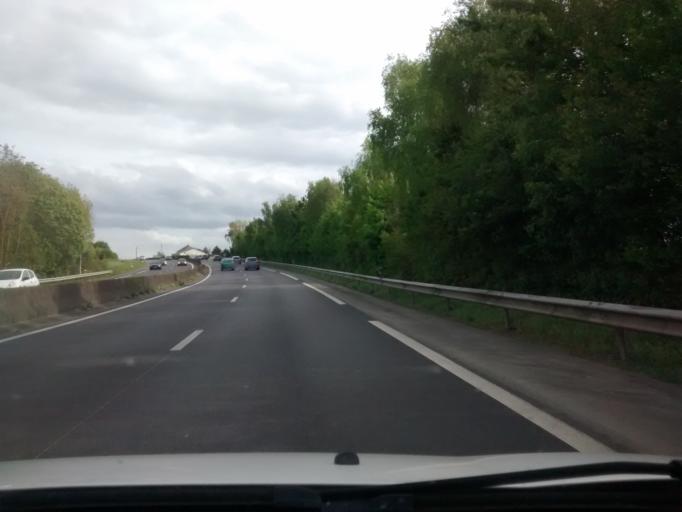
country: FR
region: Brittany
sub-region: Departement d'Ille-et-Vilaine
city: Saint-Pere
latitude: 48.5813
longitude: -1.9502
